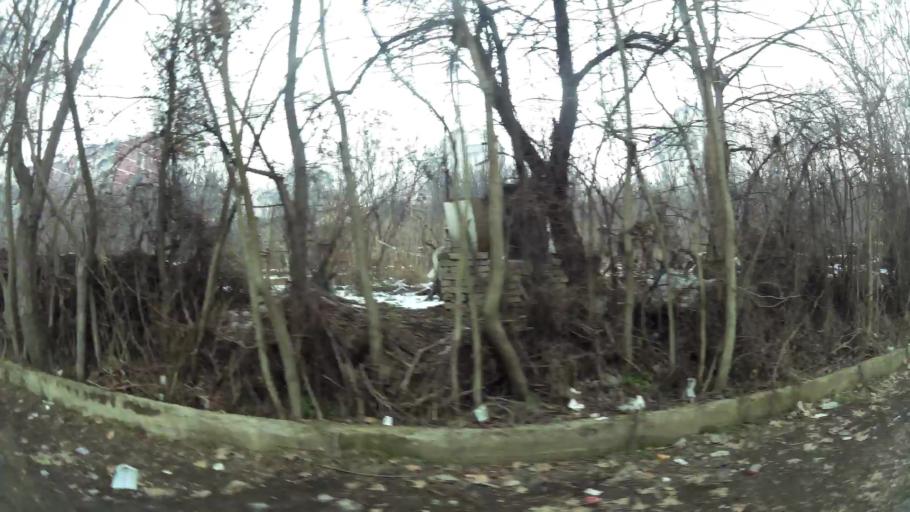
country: MK
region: Cair
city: Cair
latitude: 42.0085
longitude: 21.4607
